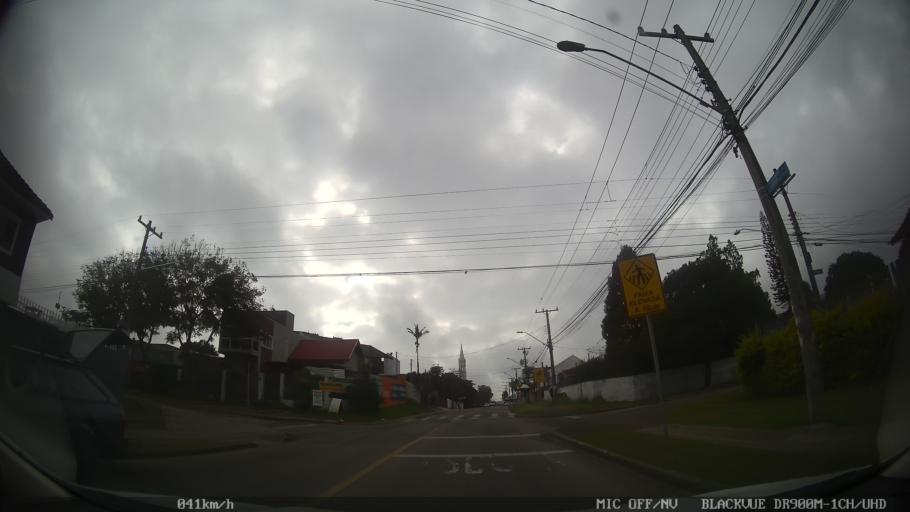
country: BR
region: Parana
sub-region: Curitiba
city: Curitiba
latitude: -25.3670
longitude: -49.2650
